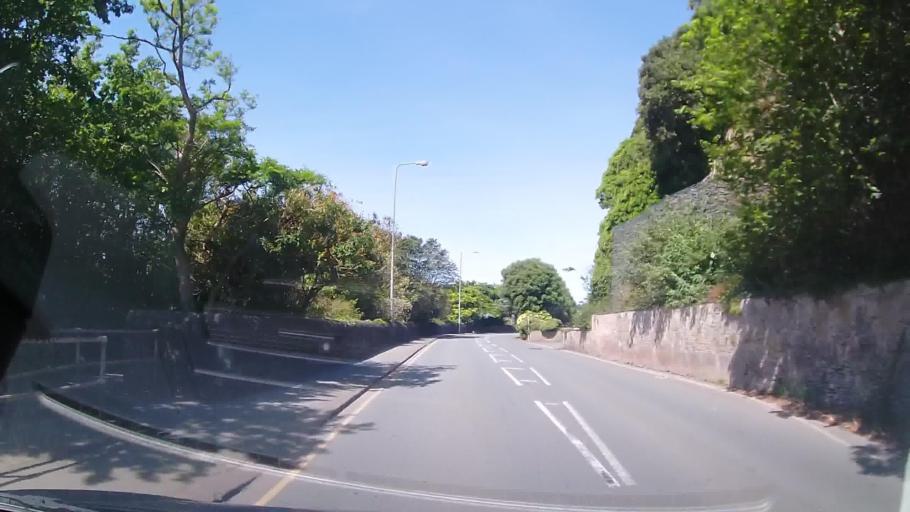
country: GB
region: Wales
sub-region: Gwynedd
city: Tywyn
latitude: 52.5440
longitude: -4.0500
